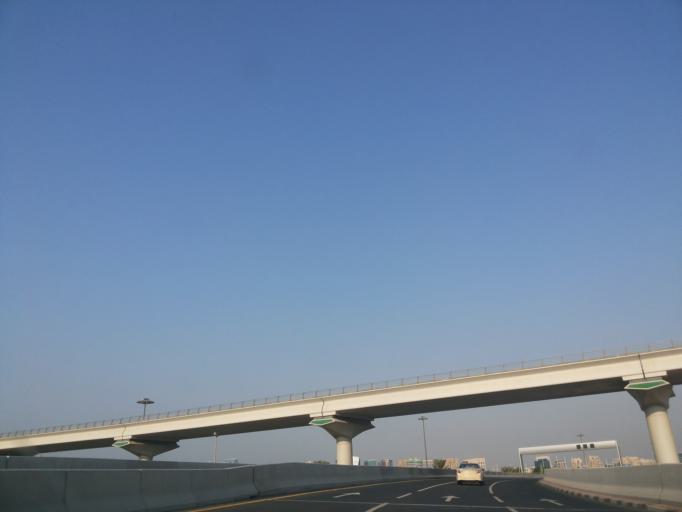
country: AE
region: Ash Shariqah
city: Sharjah
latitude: 25.2475
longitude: 55.3140
